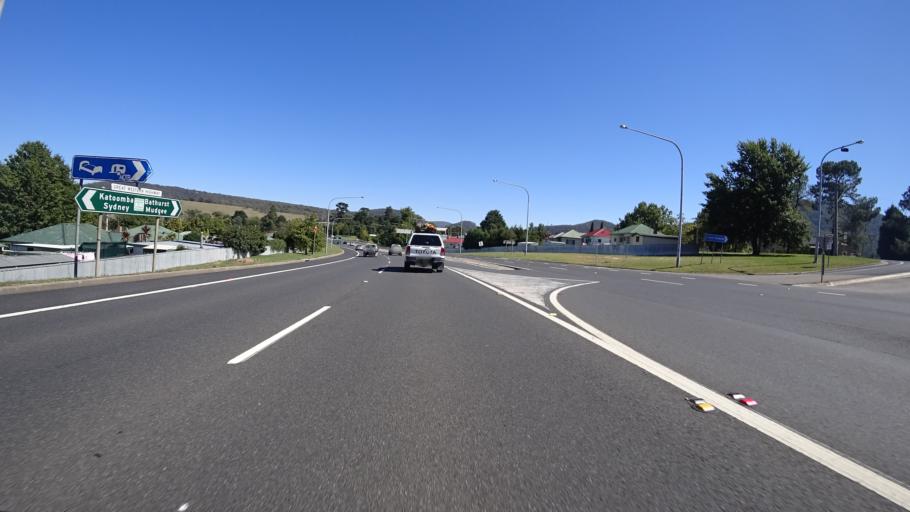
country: AU
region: New South Wales
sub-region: Lithgow
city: Lithgow
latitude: -33.4782
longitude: 150.1355
